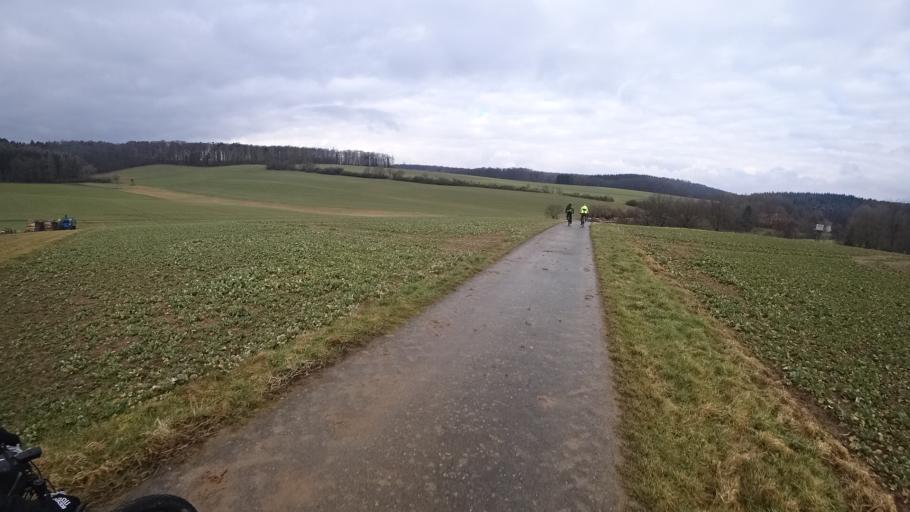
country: DE
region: Rheinland-Pfalz
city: Diethardt
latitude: 50.1660
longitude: 7.8693
